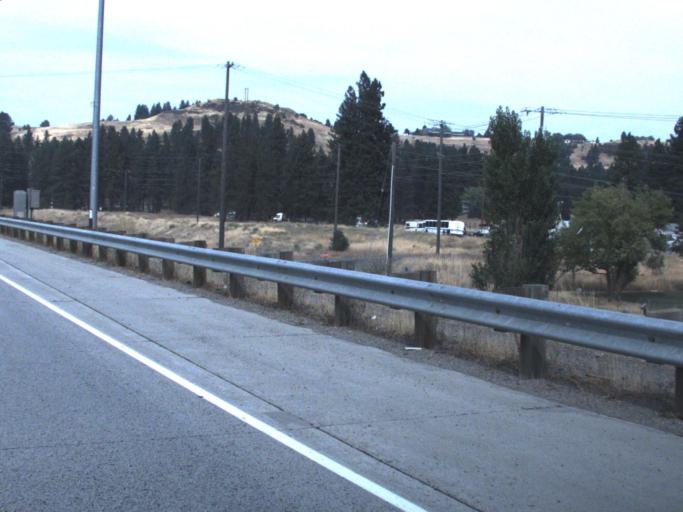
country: US
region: Washington
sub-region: Spokane County
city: Mead
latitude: 47.7192
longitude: -117.3578
